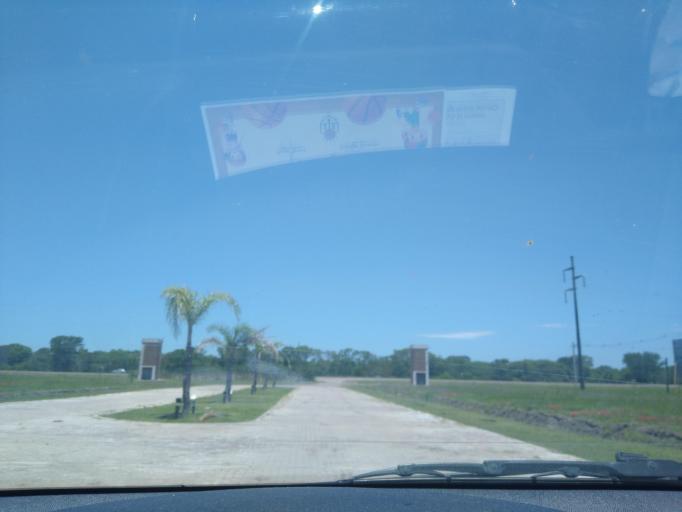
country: AR
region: Chaco
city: Makalle
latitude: -27.2520
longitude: -59.1642
